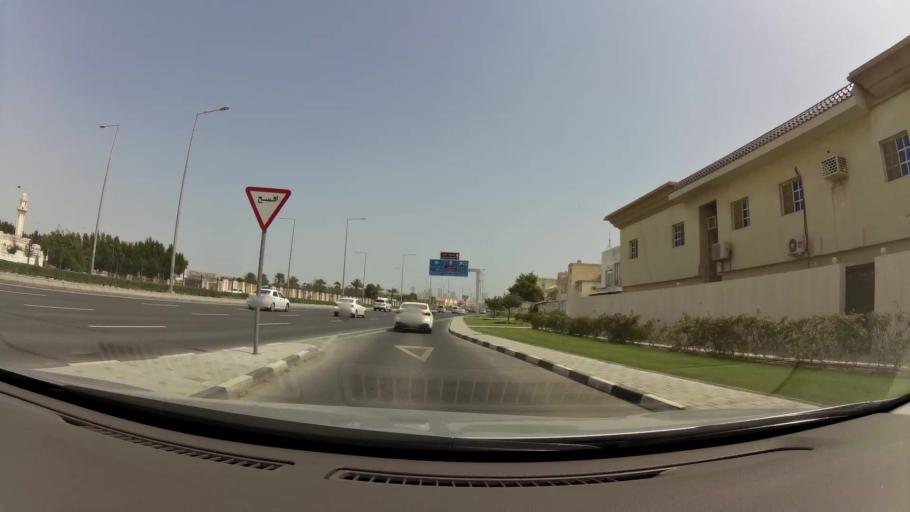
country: QA
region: Baladiyat ad Dawhah
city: Doha
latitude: 25.3227
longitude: 51.4811
